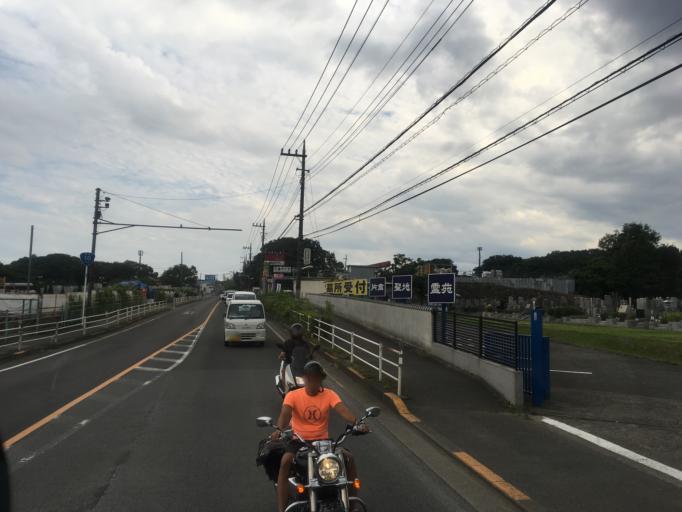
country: JP
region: Tokyo
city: Hachioji
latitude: 35.6304
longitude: 139.3379
